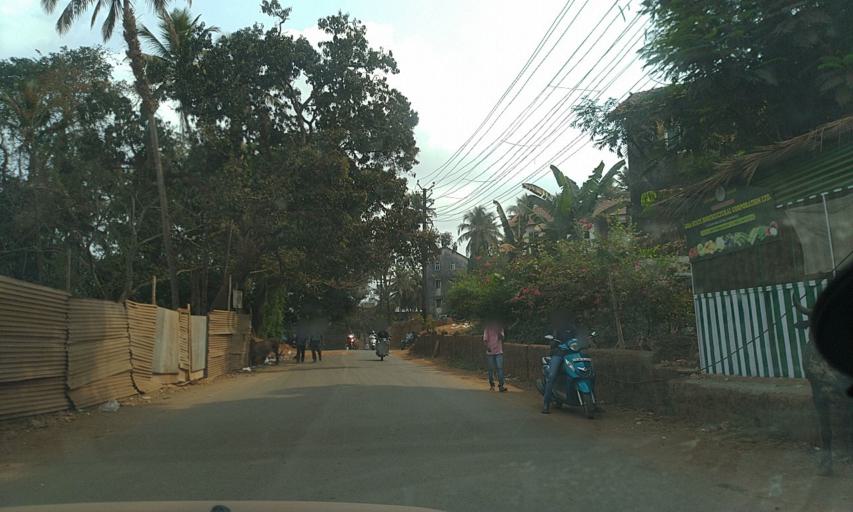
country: IN
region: Goa
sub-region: North Goa
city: Ponda
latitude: 15.4045
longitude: 74.0100
